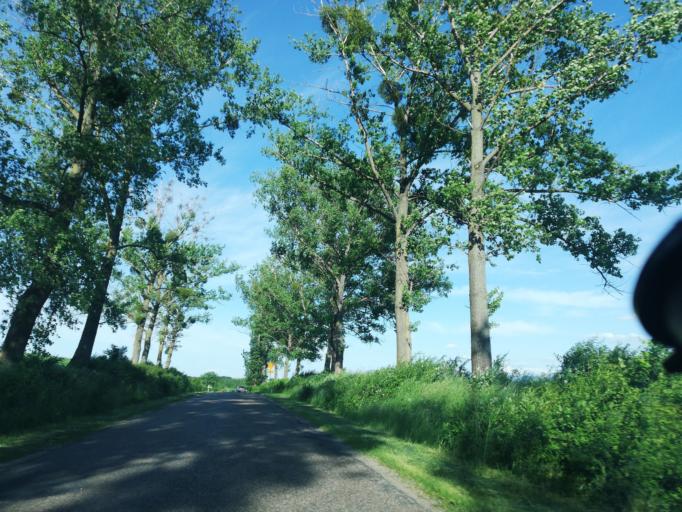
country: PL
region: Kujawsko-Pomorskie
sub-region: Powiat golubsko-dobrzynski
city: Zbojno
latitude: 53.0400
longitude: 19.0949
